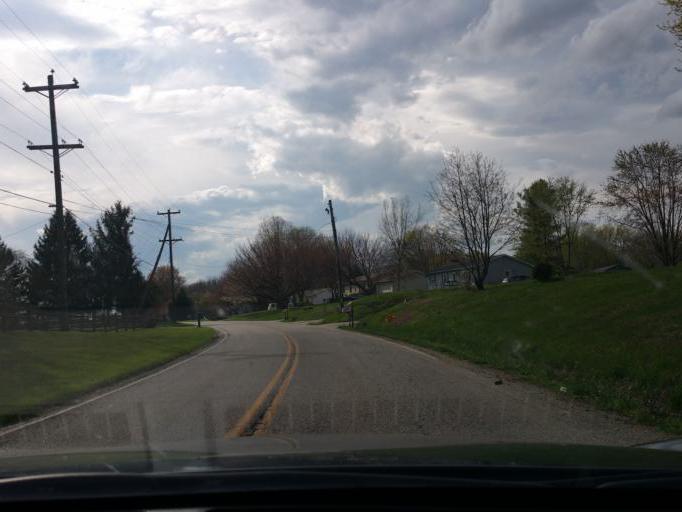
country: US
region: Maryland
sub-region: Cecil County
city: Rising Sun
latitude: 39.6410
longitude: -76.1226
